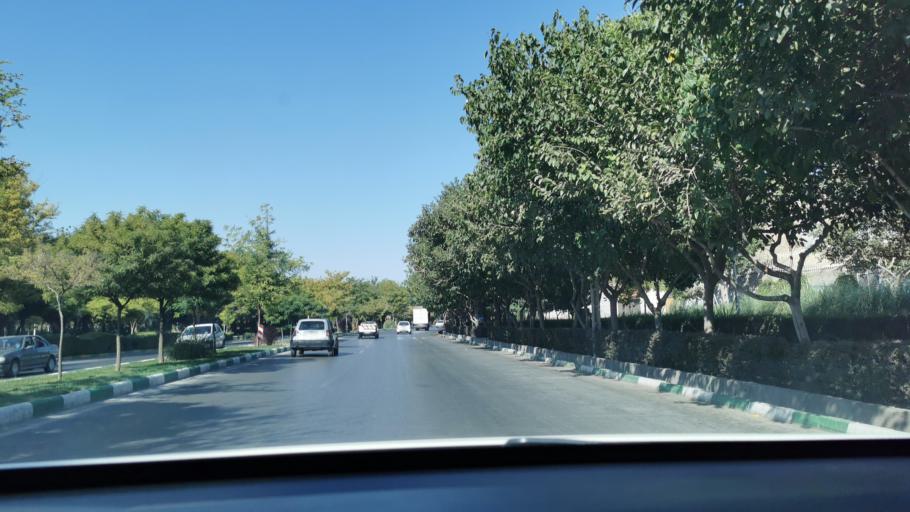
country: IR
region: Razavi Khorasan
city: Mashhad
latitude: 36.3351
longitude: 59.6307
